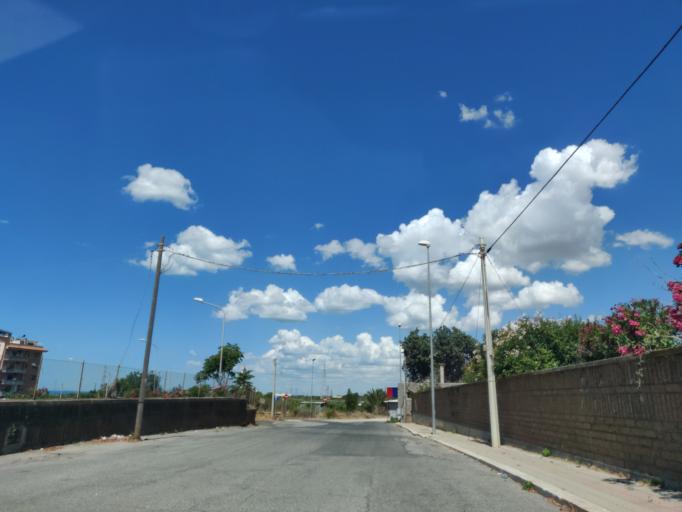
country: IT
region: Latium
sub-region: Citta metropolitana di Roma Capitale
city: Civitavecchia
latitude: 42.1035
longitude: 11.7968
